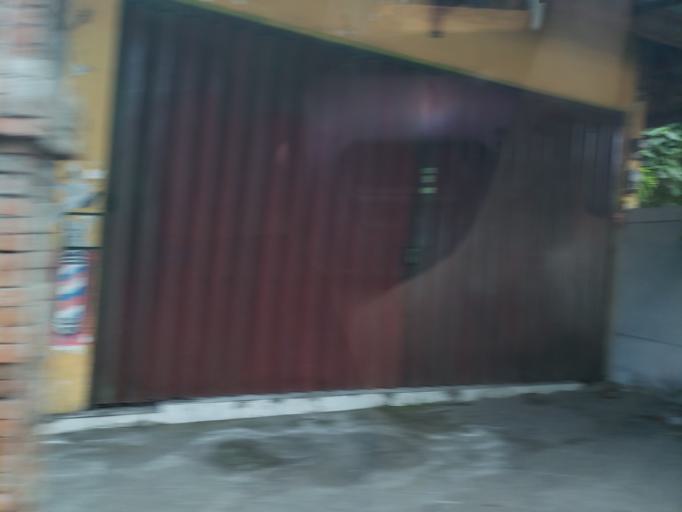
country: ID
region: Bali
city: Kangin
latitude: -8.8258
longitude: 115.1509
